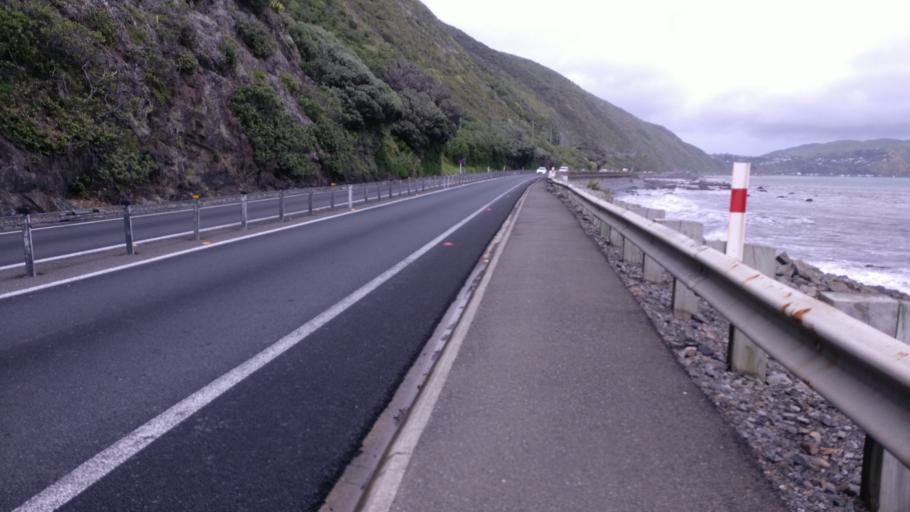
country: NZ
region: Wellington
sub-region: Kapiti Coast District
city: Paraparaumu
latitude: -41.0094
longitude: 174.9234
